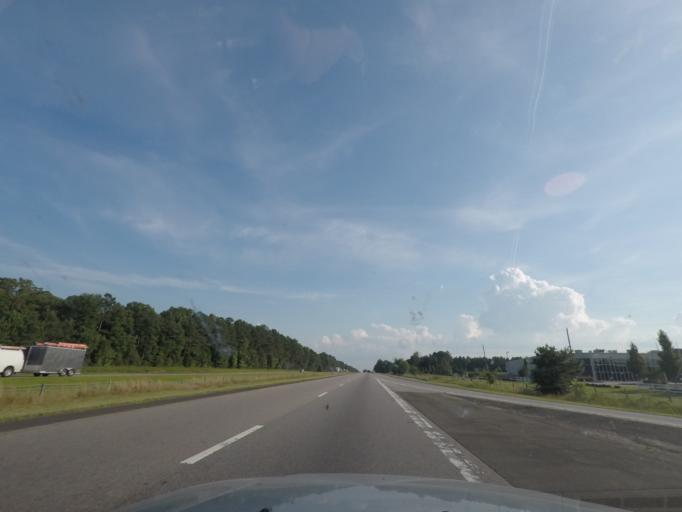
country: US
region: North Carolina
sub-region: Granville County
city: Butner
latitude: 36.1186
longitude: -78.7471
